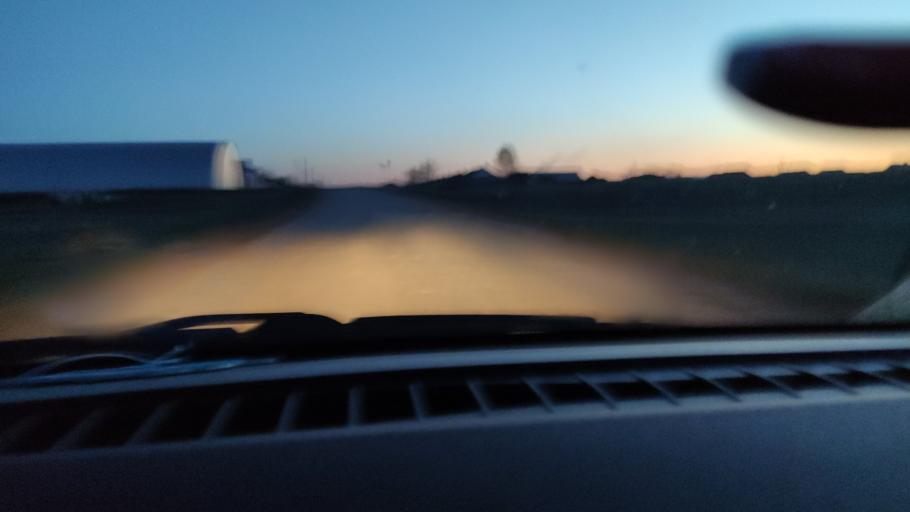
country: RU
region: Saratov
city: Rovnoye
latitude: 50.9330
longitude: 46.0923
